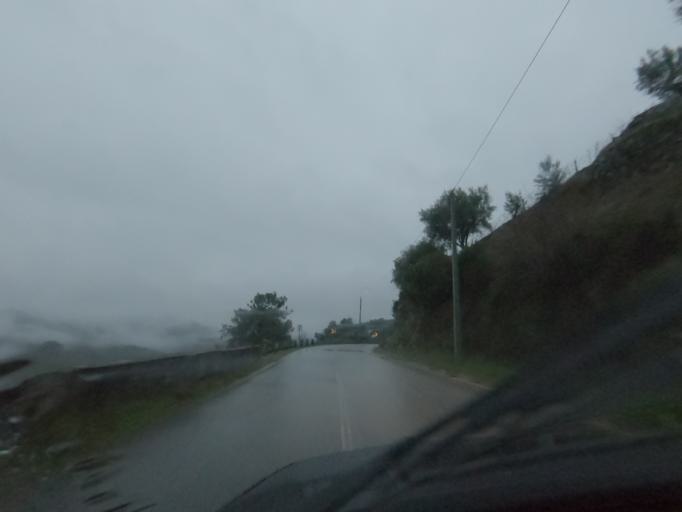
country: PT
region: Vila Real
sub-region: Sabrosa
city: Vilela
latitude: 41.2229
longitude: -7.5549
